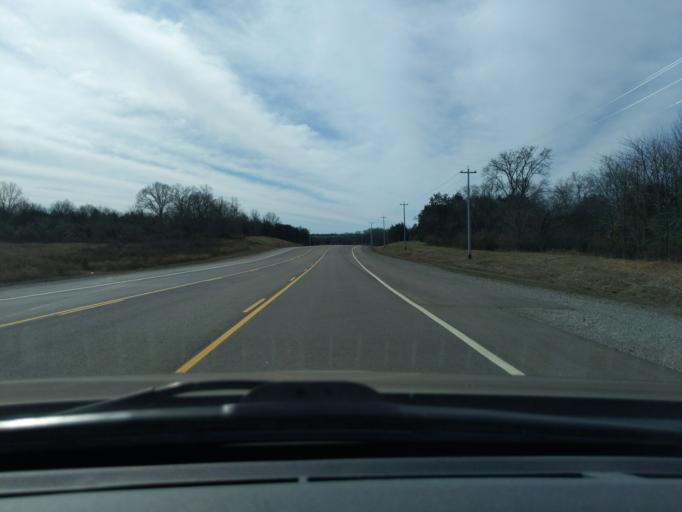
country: US
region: Tennessee
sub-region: Wilson County
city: Mount Juliet
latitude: 36.2100
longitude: -86.4968
